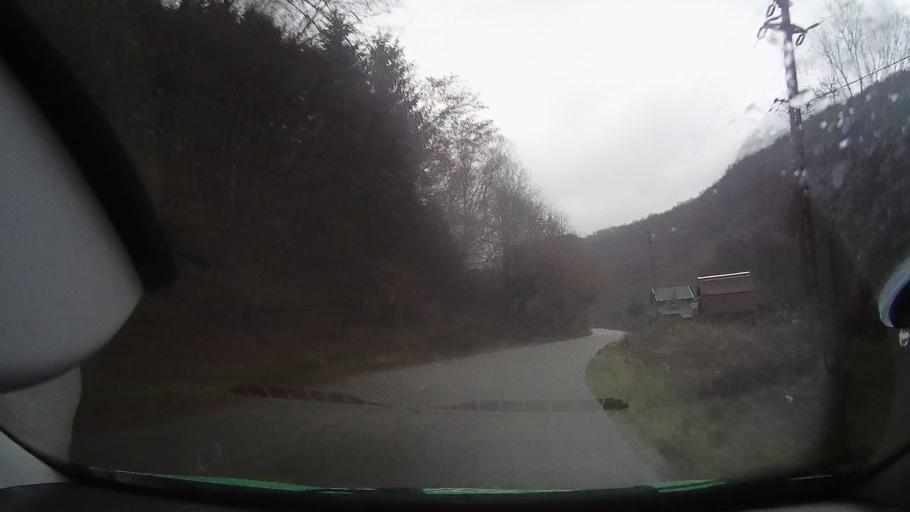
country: RO
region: Alba
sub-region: Comuna Avram Iancu
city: Avram Iancu
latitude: 46.2904
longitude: 22.7507
